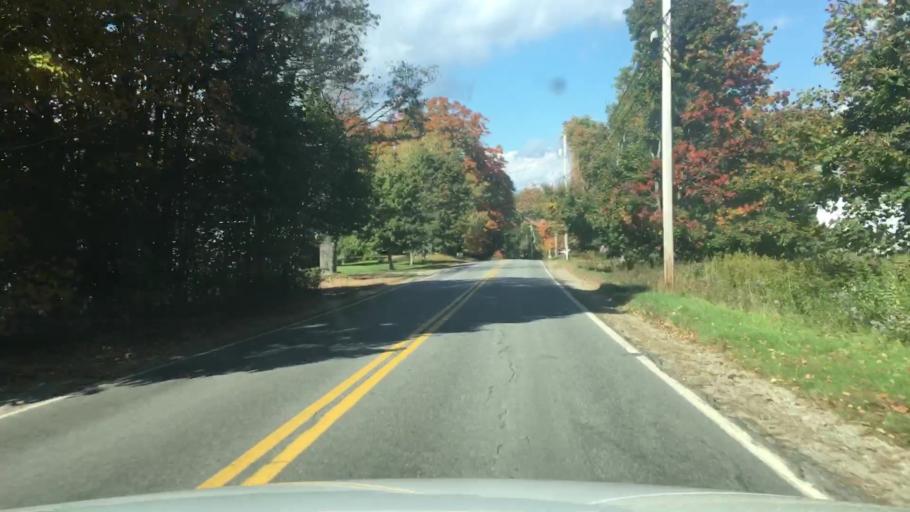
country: US
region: Maine
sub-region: Knox County
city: Warren
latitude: 44.1160
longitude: -69.2321
